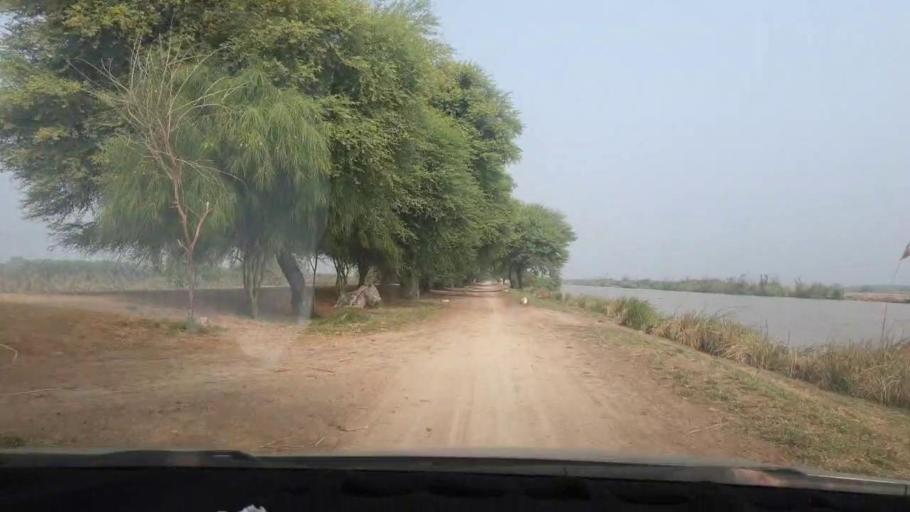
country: PK
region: Sindh
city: Tando Adam
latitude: 25.6762
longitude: 68.5574
